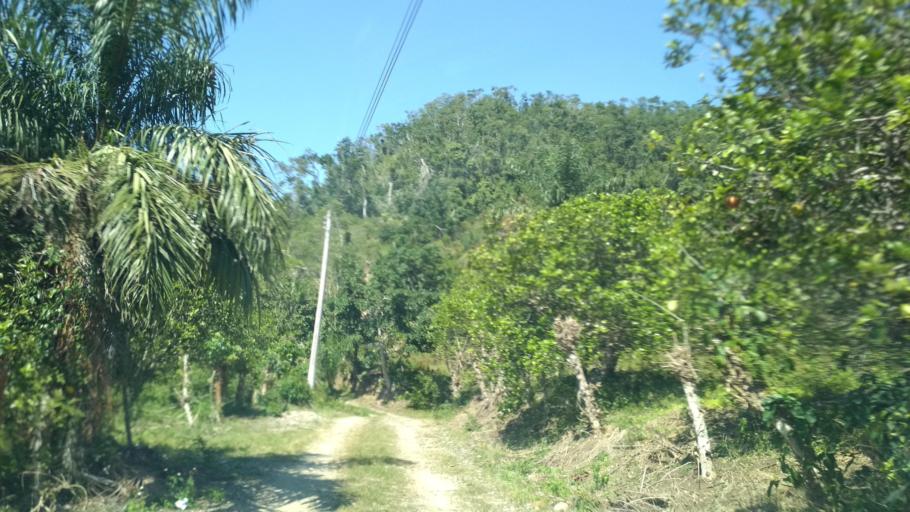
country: MX
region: Veracruz
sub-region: Papantla
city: Polutla
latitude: 20.4888
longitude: -97.2298
